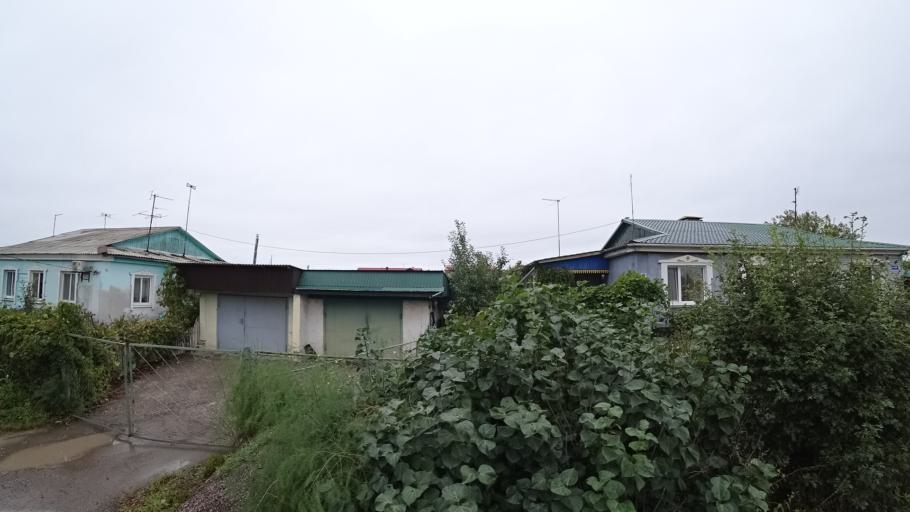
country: RU
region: Primorskiy
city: Monastyrishche
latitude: 44.2034
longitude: 132.4299
